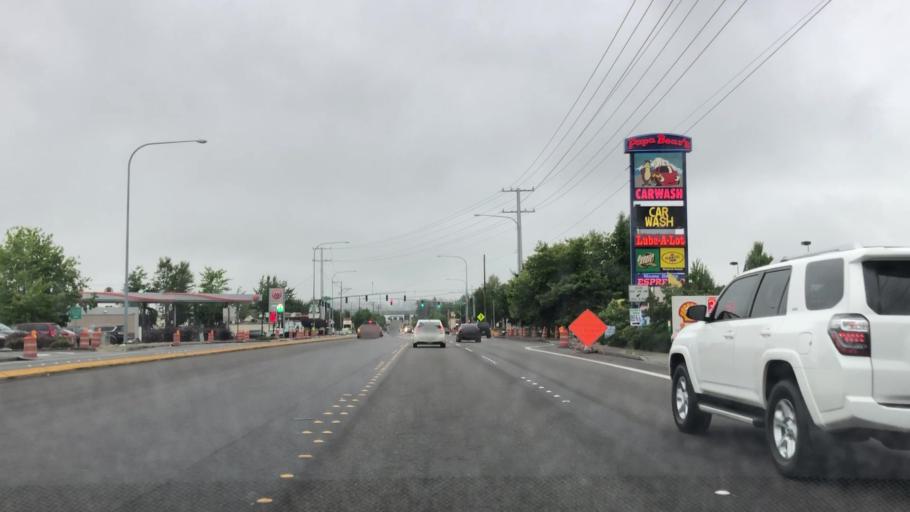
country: US
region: Washington
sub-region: Snohomish County
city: North Creek
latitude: 47.8110
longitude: -122.2069
